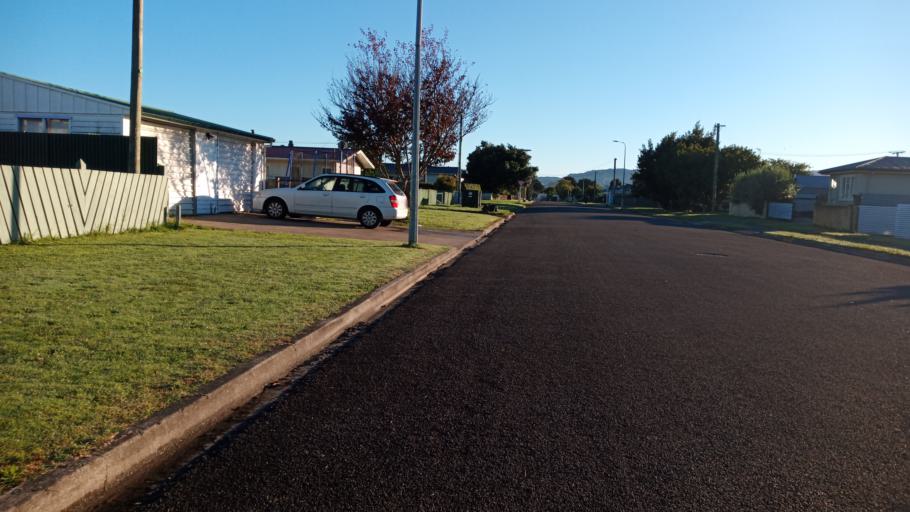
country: NZ
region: Gisborne
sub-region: Gisborne District
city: Gisborne
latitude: -38.6615
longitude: 177.9889
